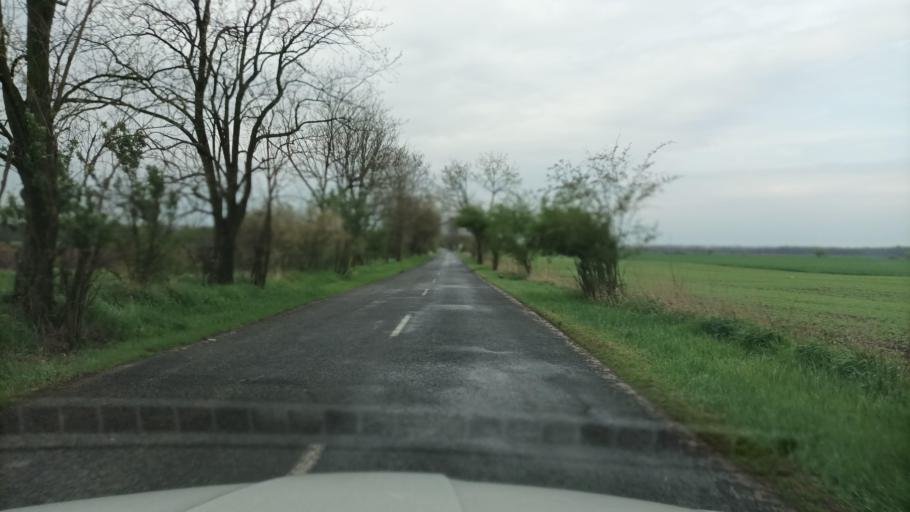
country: HU
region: Pest
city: Danszentmiklos
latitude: 47.1824
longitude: 19.5370
